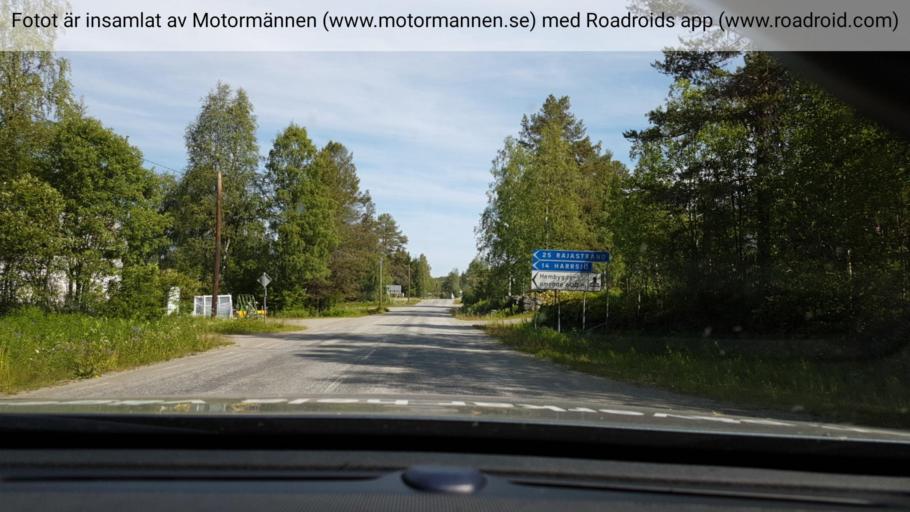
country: SE
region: Vaesterbotten
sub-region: Vilhelmina Kommun
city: Sjoberg
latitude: 64.5734
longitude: 15.8730
